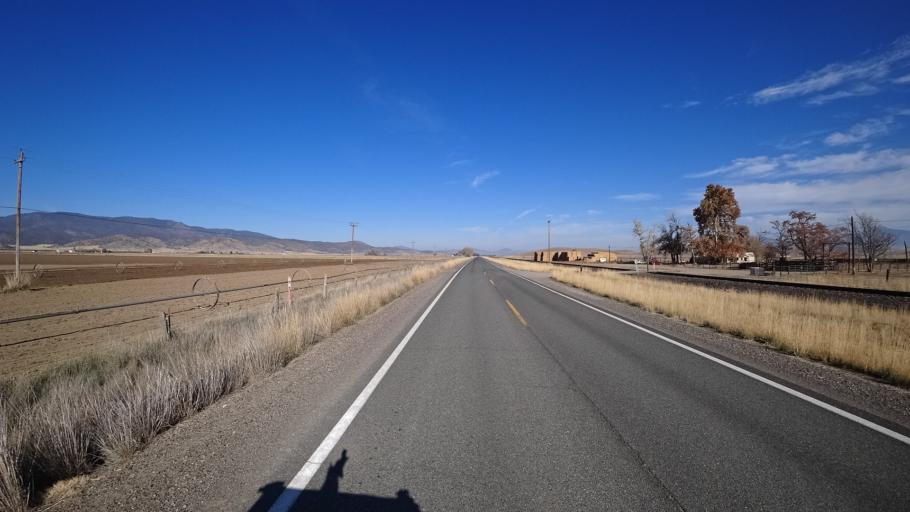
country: US
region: California
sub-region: Siskiyou County
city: Weed
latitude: 41.5430
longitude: -122.5258
